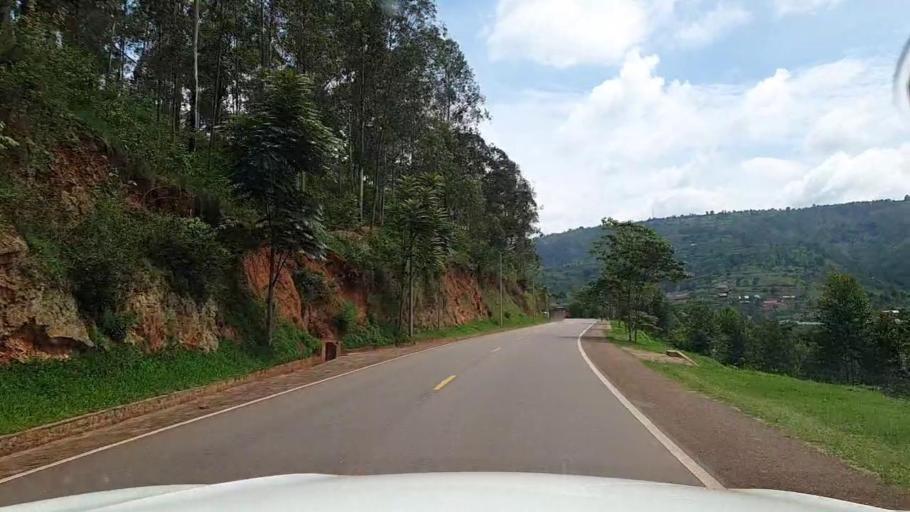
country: RW
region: Kigali
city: Kigali
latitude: -1.8598
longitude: 30.0918
